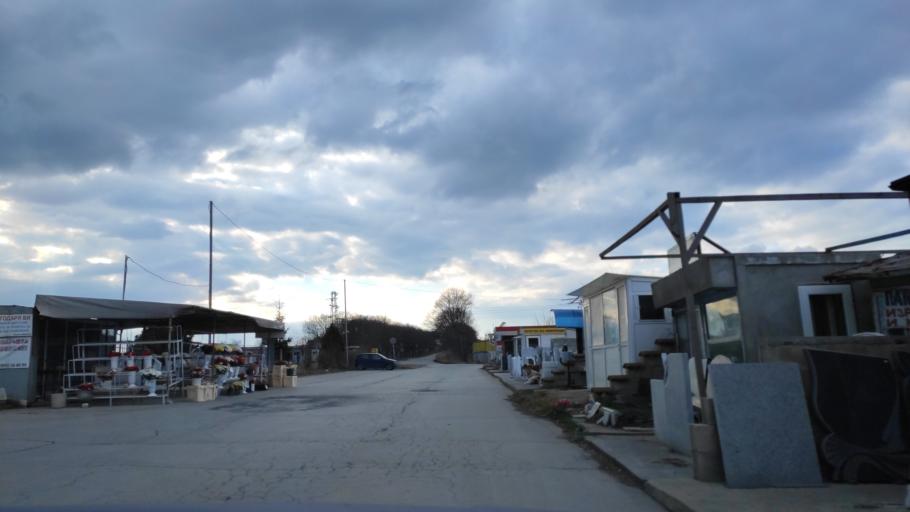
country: BG
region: Varna
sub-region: Obshtina Aksakovo
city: Aksakovo
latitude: 43.2245
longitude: 27.8058
